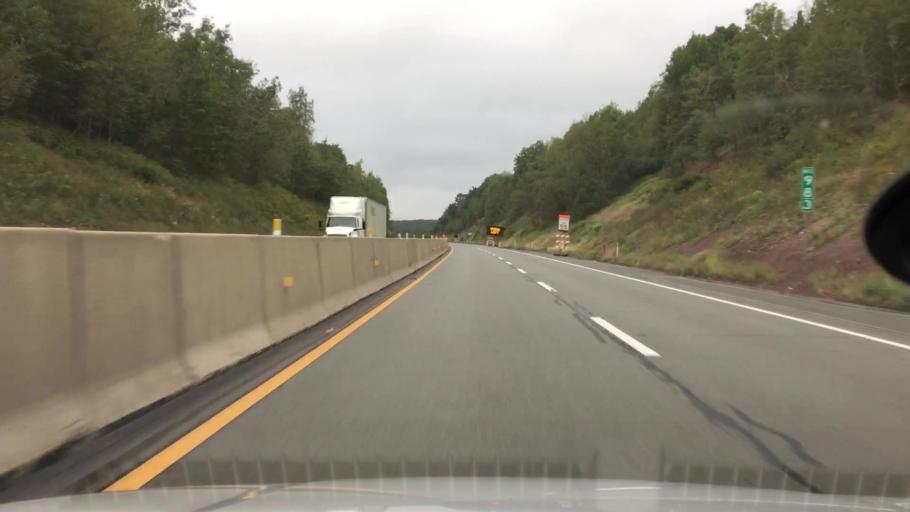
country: US
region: Pennsylvania
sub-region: Luzerne County
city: White Haven
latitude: 41.1071
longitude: -75.7520
